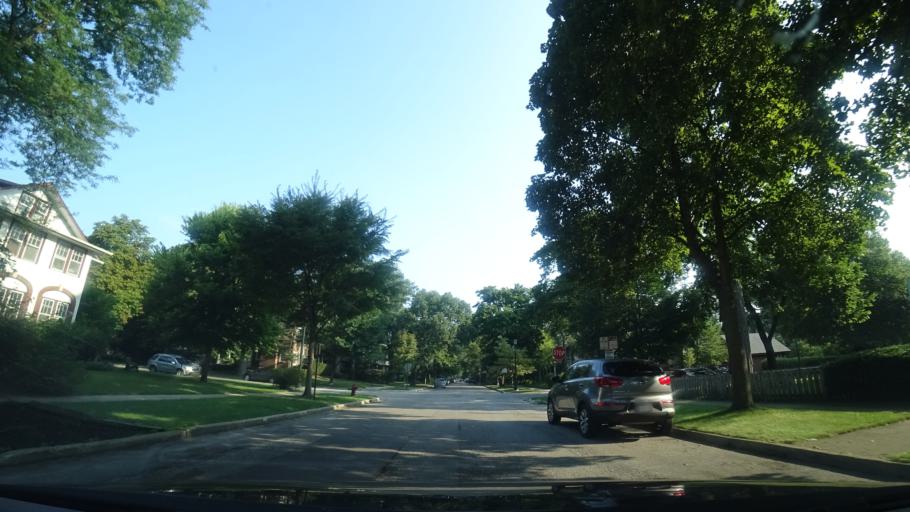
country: US
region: Illinois
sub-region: Cook County
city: Evanston
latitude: 42.0355
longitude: -87.6852
